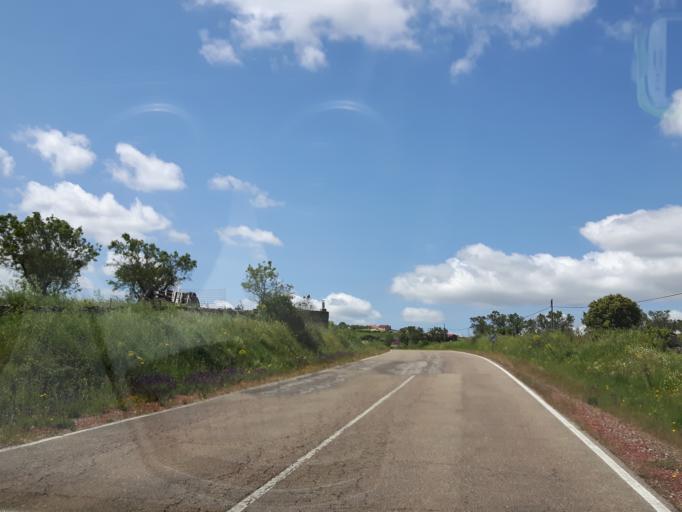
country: ES
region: Castille and Leon
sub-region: Provincia de Salamanca
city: Aldea del Obispo
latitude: 40.7124
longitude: -6.7873
